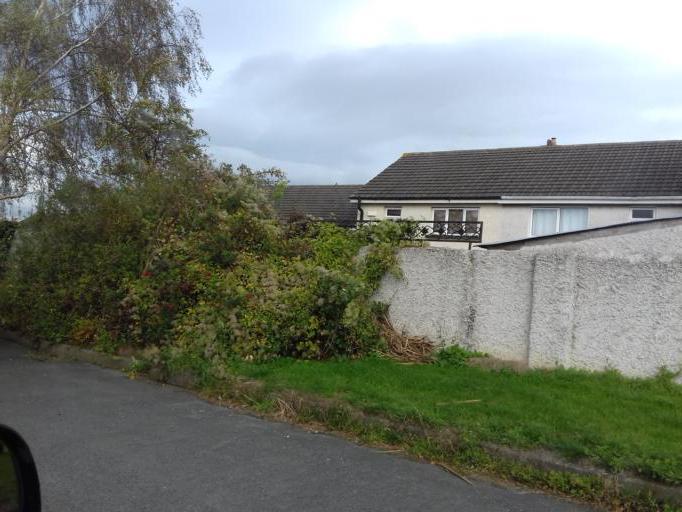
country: IE
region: Leinster
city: Little Bray
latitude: 53.1901
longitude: -6.1292
